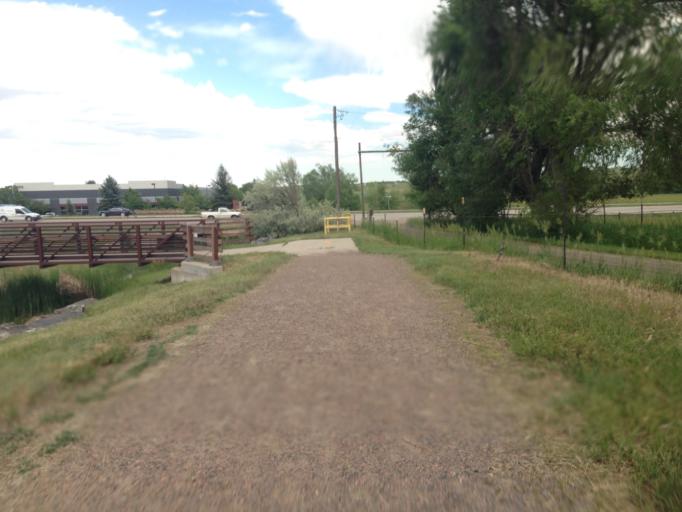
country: US
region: Colorado
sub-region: Boulder County
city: Lafayette
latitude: 39.9652
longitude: -105.0914
